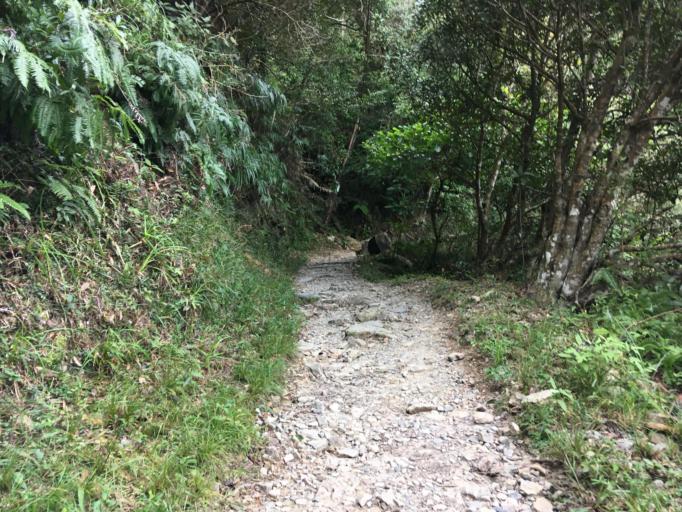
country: TW
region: Taiwan
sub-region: Yilan
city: Yilan
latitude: 24.8444
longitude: 121.7773
